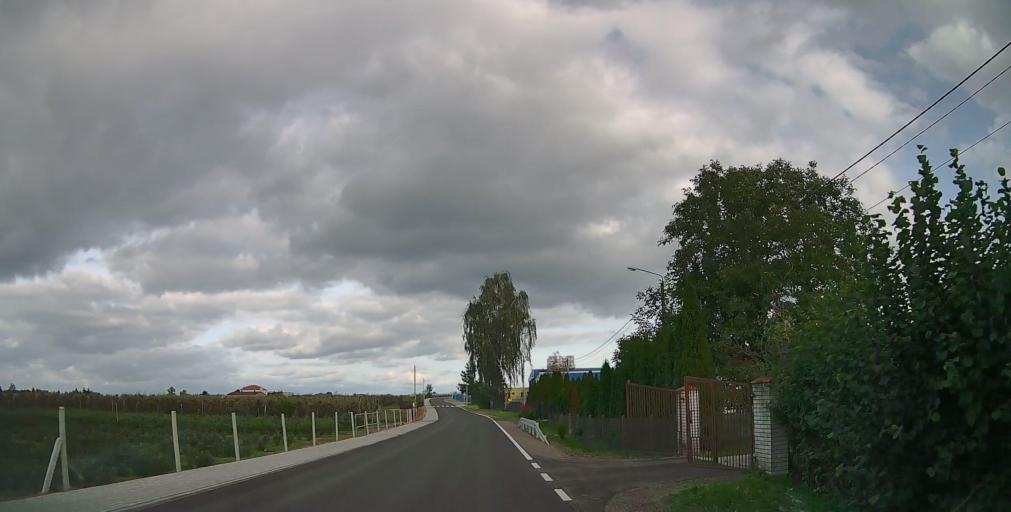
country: PL
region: Masovian Voivodeship
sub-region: Powiat bialobrzeski
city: Promna
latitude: 51.7089
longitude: 20.9520
